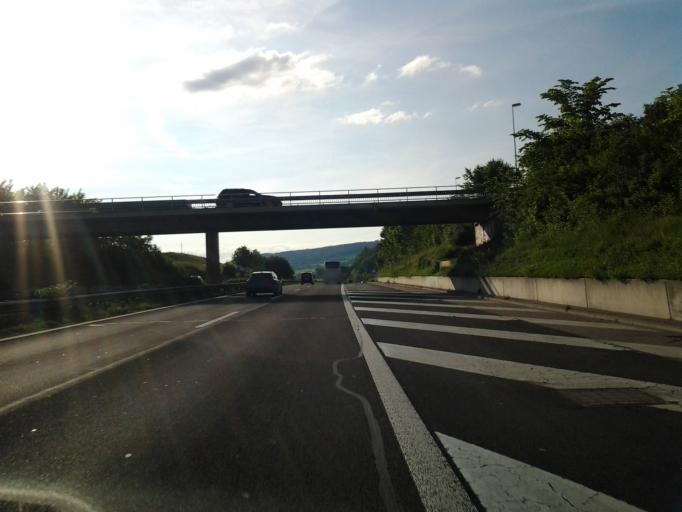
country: CH
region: Lucerne
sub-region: Sursee District
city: Knutwil
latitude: 47.1943
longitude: 8.0707
